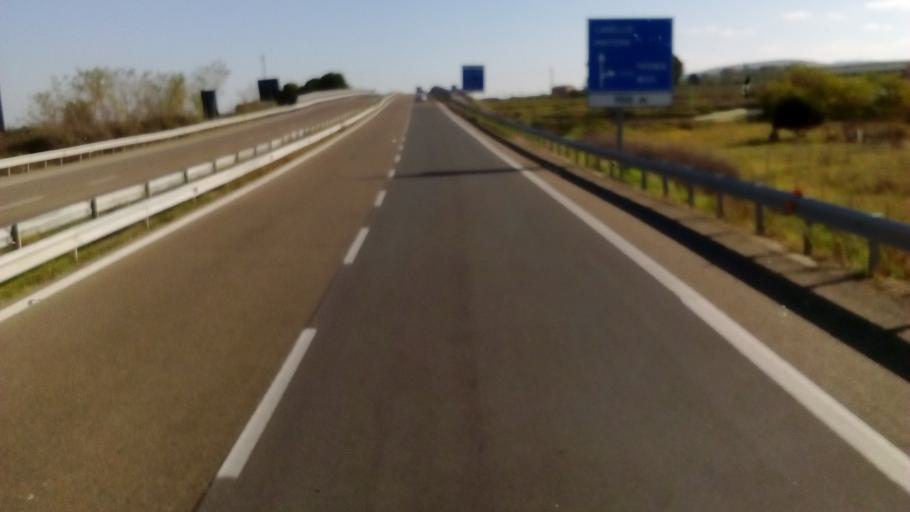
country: IT
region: Basilicate
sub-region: Provincia di Potenza
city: Zona 179
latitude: 41.0869
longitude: 15.5991
